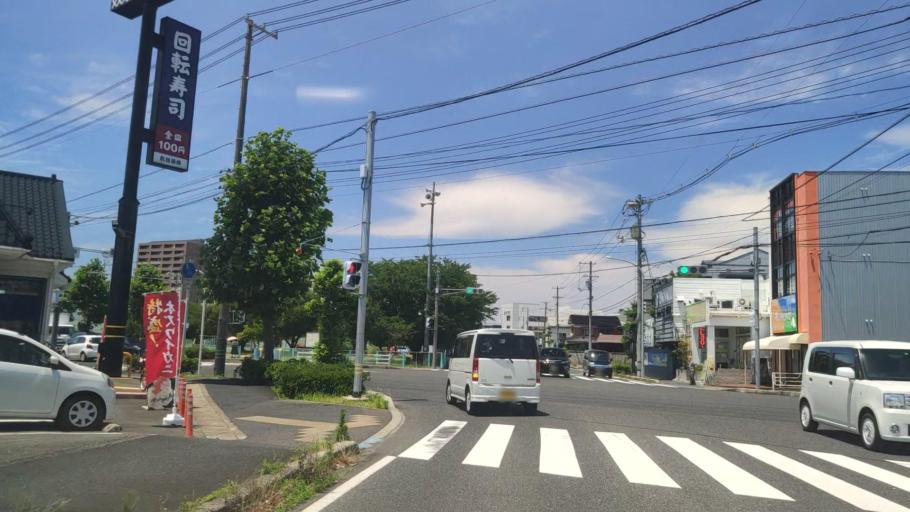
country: JP
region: Tottori
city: Tottori
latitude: 35.4883
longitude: 134.2323
